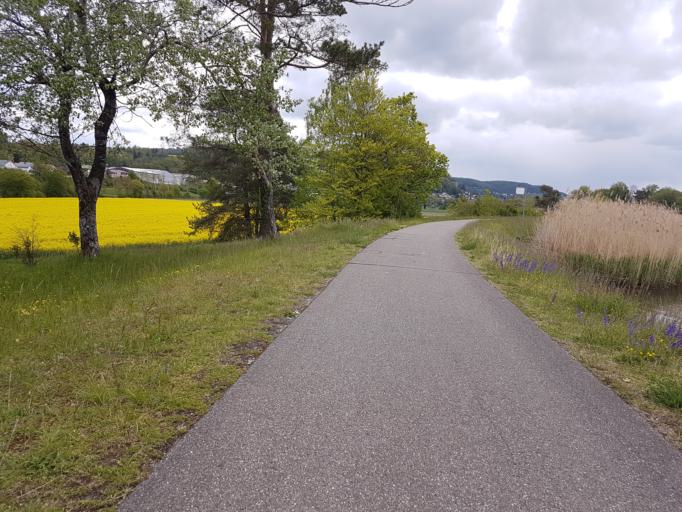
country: CH
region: Aargau
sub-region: Bezirk Zurzach
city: Koblenz
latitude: 47.5947
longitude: 8.2275
